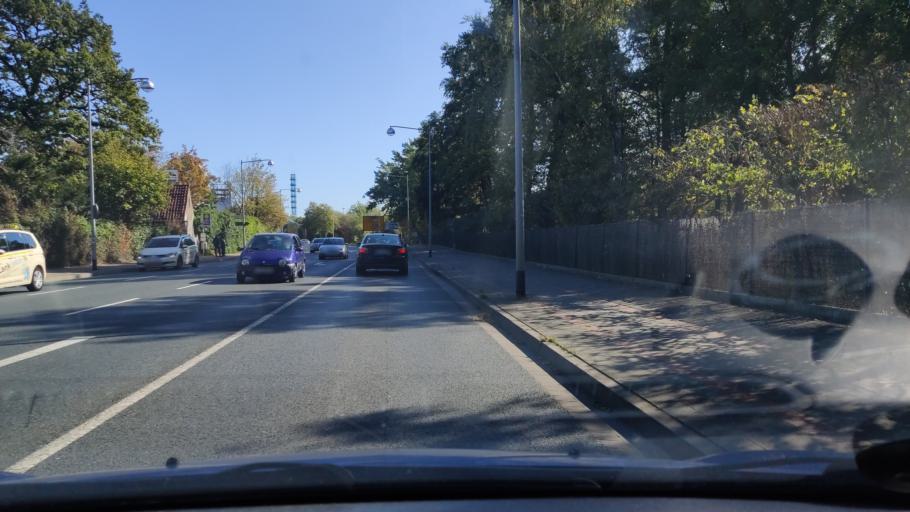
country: DE
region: Lower Saxony
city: Laatzen
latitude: 52.3180
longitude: 9.8069
